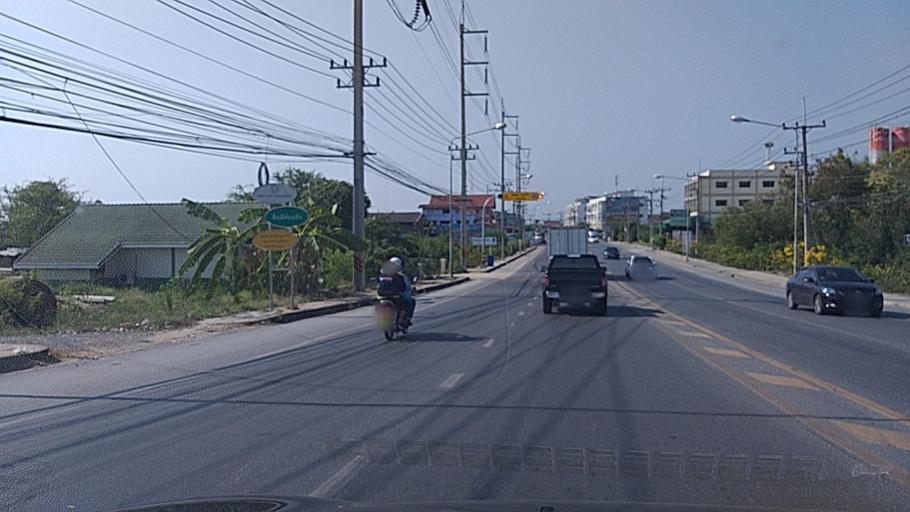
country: TH
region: Nakhon Pathom
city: Salaya
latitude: 13.8348
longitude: 100.3099
